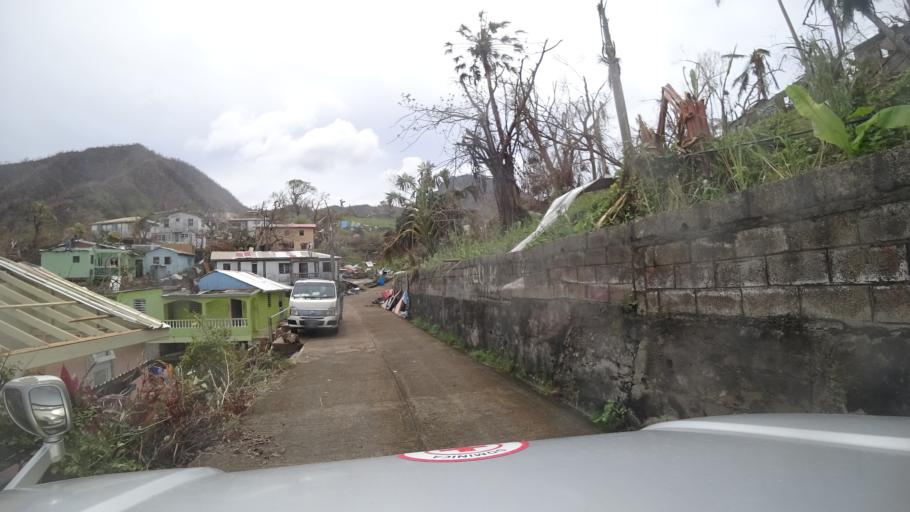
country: DM
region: Saint Andrew
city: Calibishie
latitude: 15.6138
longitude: -61.4073
